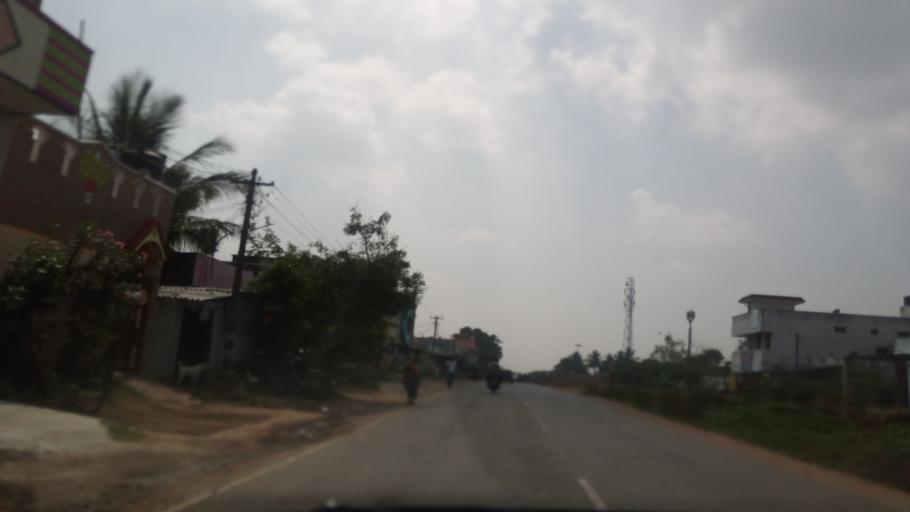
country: IN
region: Tamil Nadu
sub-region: Vellore
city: Arakkonam
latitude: 13.0586
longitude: 79.6741
